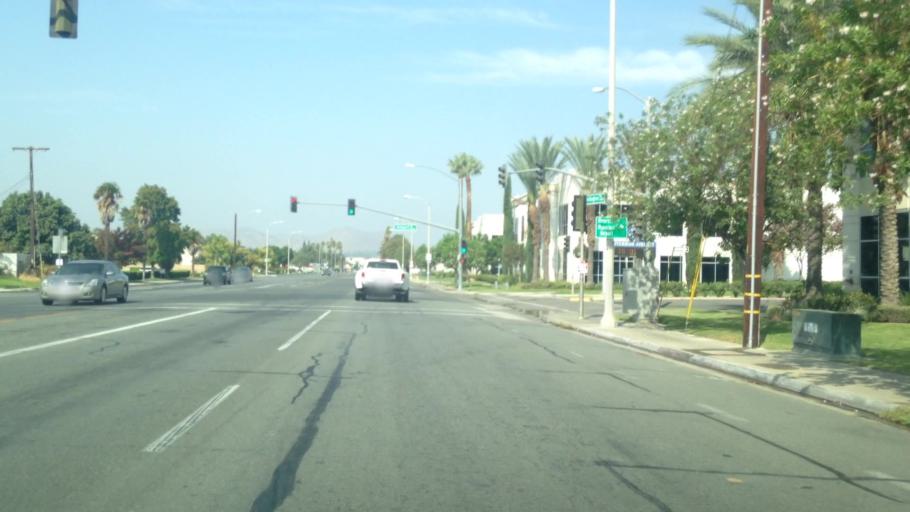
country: US
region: California
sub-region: Riverside County
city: Pedley
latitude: 33.9460
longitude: -117.4447
